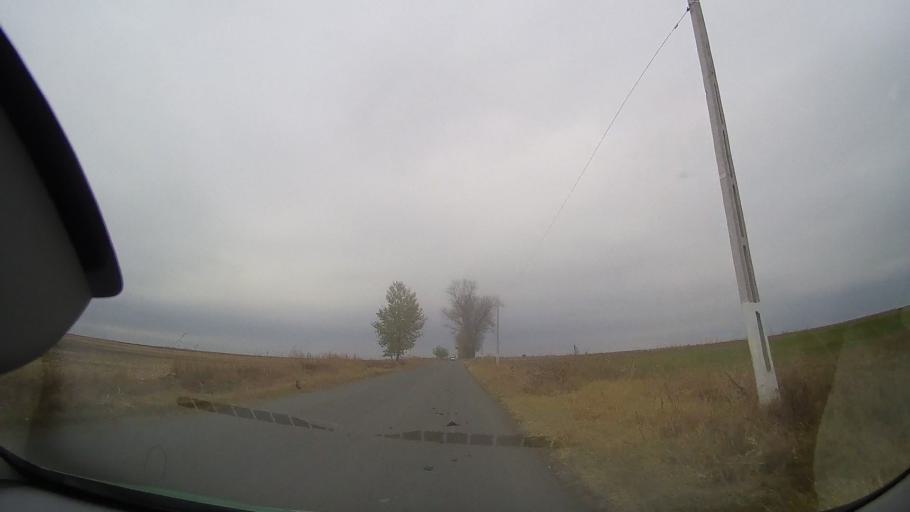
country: RO
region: Braila
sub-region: Comuna Budesti
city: Tataru
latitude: 44.8641
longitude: 27.4261
